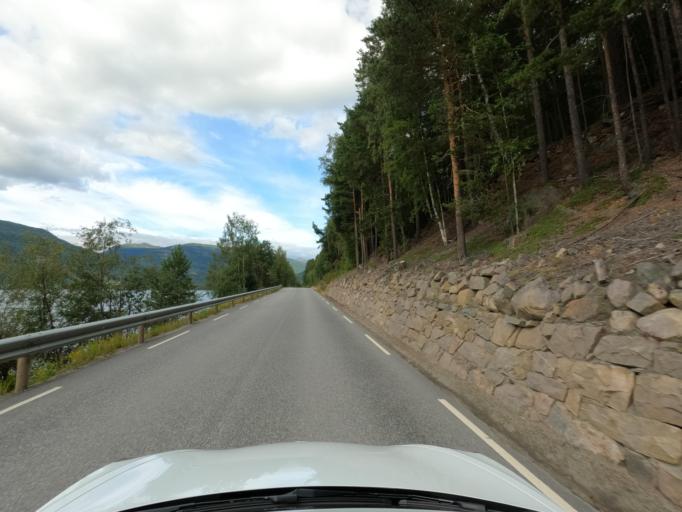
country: NO
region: Telemark
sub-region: Tinn
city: Rjukan
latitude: 59.9871
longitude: 8.7932
